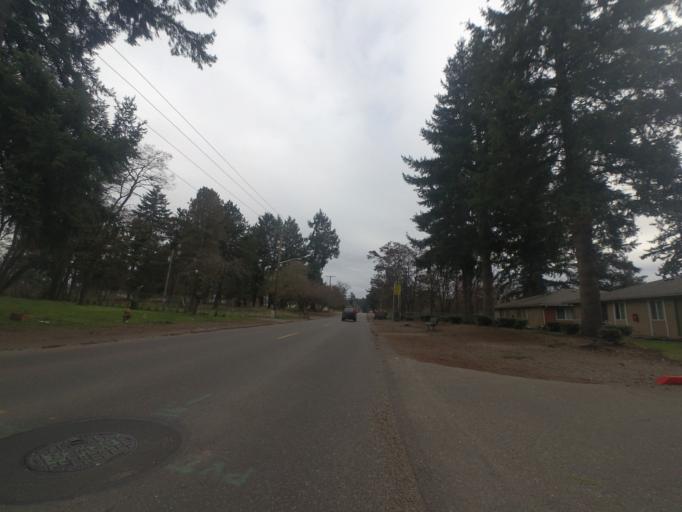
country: US
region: Washington
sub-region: Pierce County
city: McChord Air Force Base
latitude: 47.1248
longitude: -122.5340
